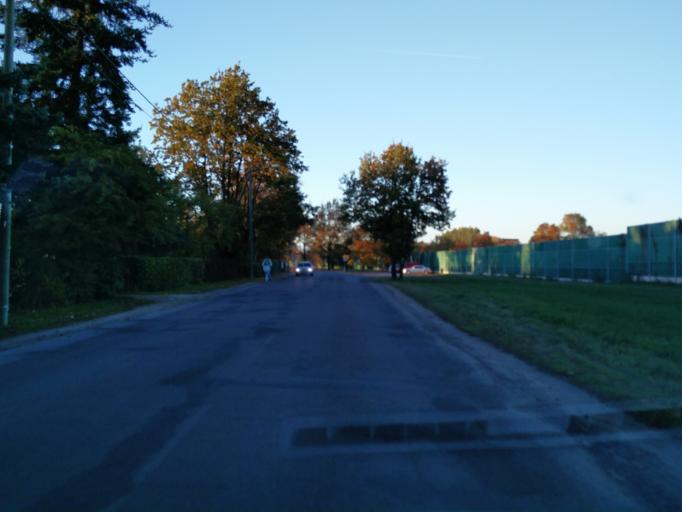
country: EE
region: Tartu
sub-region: Tartu linn
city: Tartu
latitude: 58.3640
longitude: 26.7169
